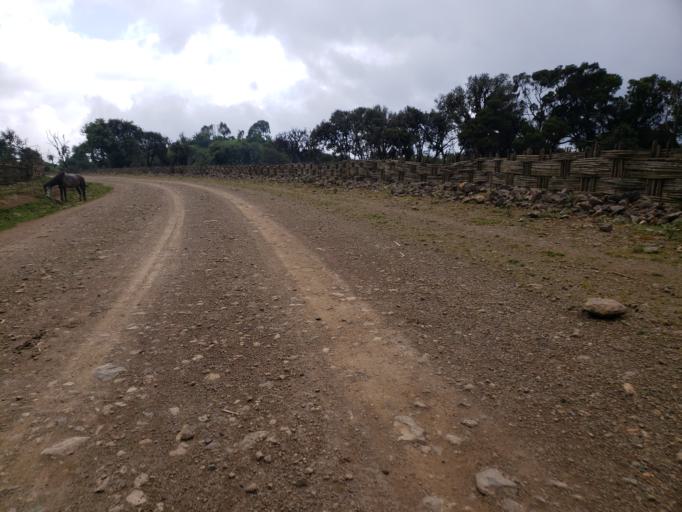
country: ET
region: Oromiya
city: Dodola
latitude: 6.7099
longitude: 39.3735
